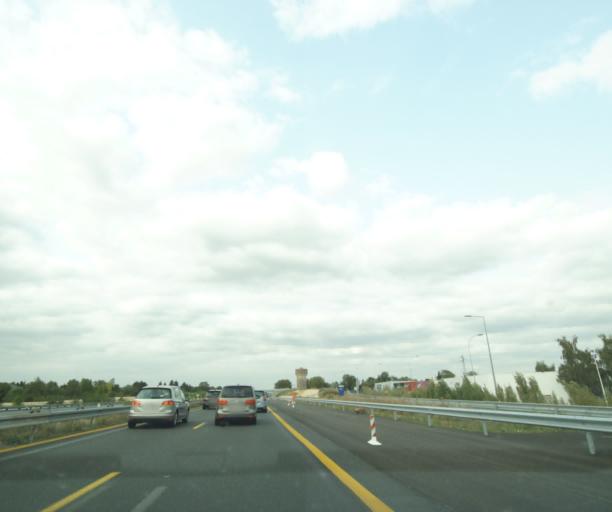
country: FR
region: Centre
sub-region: Departement d'Indre-et-Loire
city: Chambray-les-Tours
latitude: 47.3408
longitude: 0.6984
